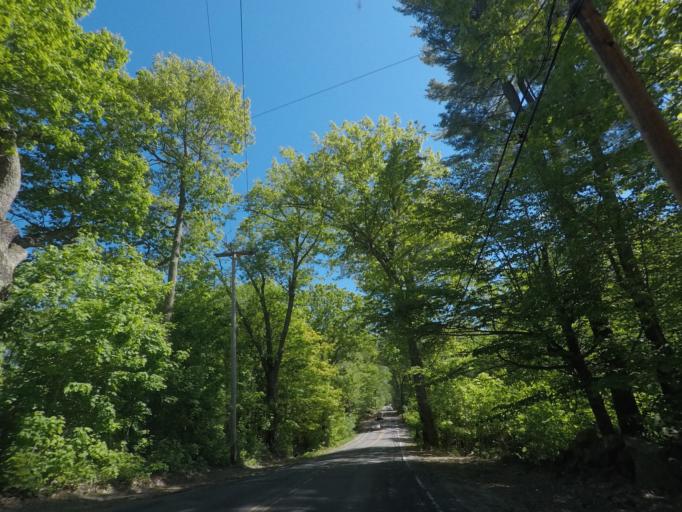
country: US
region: Maine
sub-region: Kennebec County
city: Manchester
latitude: 44.2765
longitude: -69.8976
